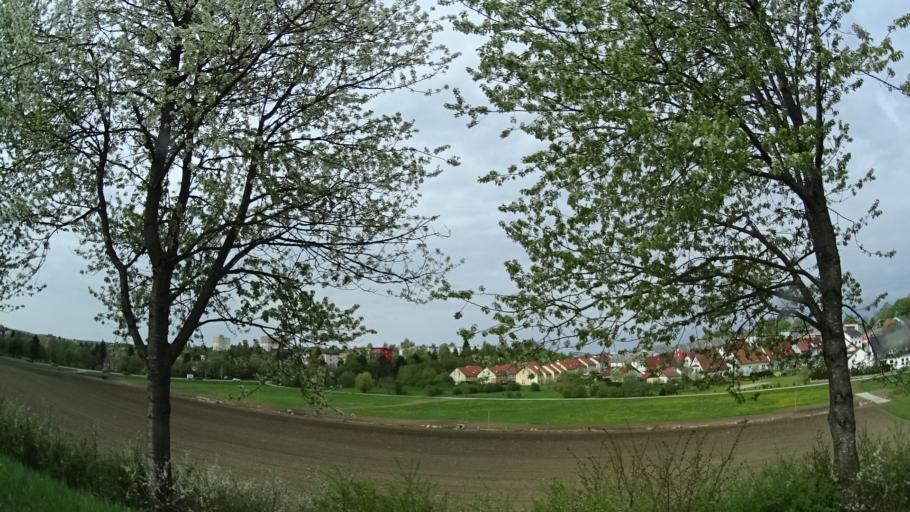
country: DE
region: Baden-Wuerttemberg
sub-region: Freiburg Region
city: Villingen-Schwenningen
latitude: 48.0707
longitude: 8.4742
